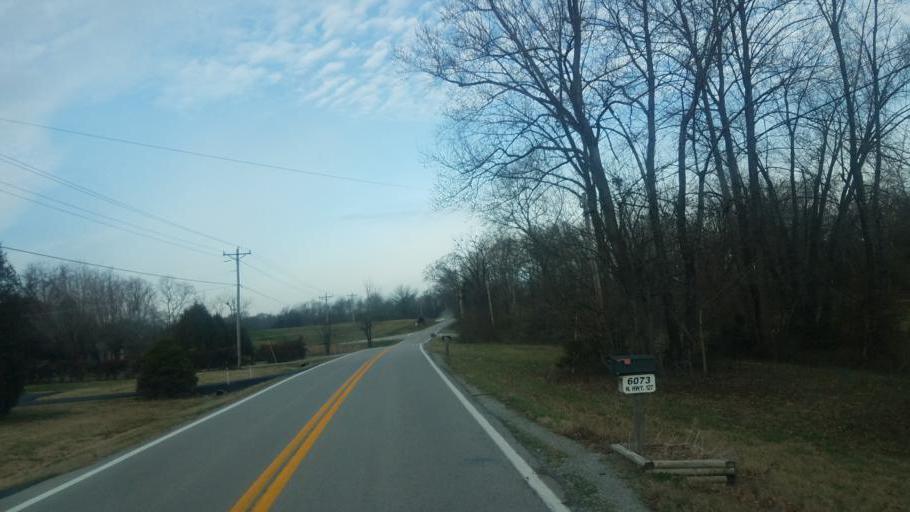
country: US
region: Kentucky
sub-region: Clinton County
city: Albany
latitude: 36.7591
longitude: -85.1569
